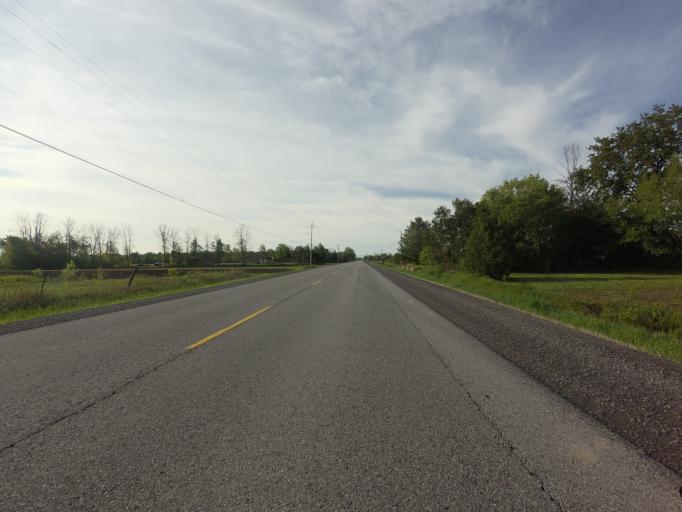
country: CA
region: Ontario
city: Ottawa
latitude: 45.2949
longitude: -75.4508
